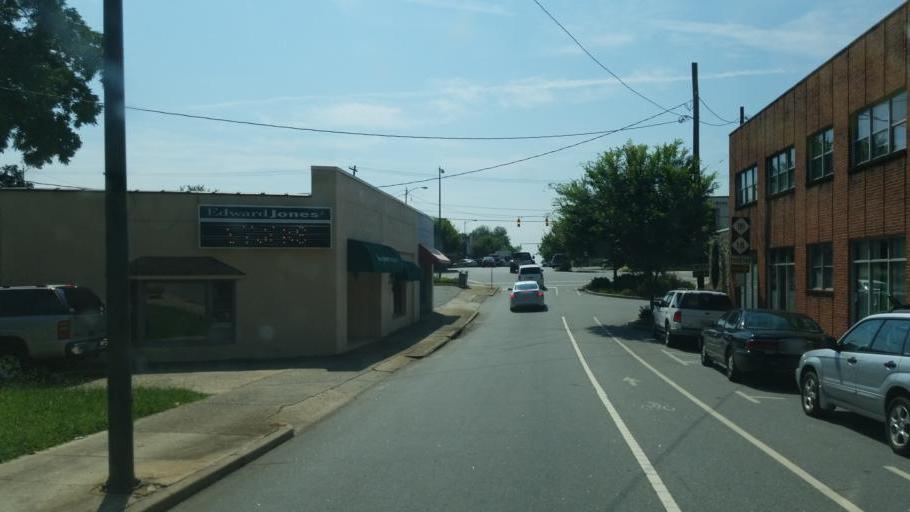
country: US
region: North Carolina
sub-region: Burke County
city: Morganton
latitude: 35.7473
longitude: -81.6907
